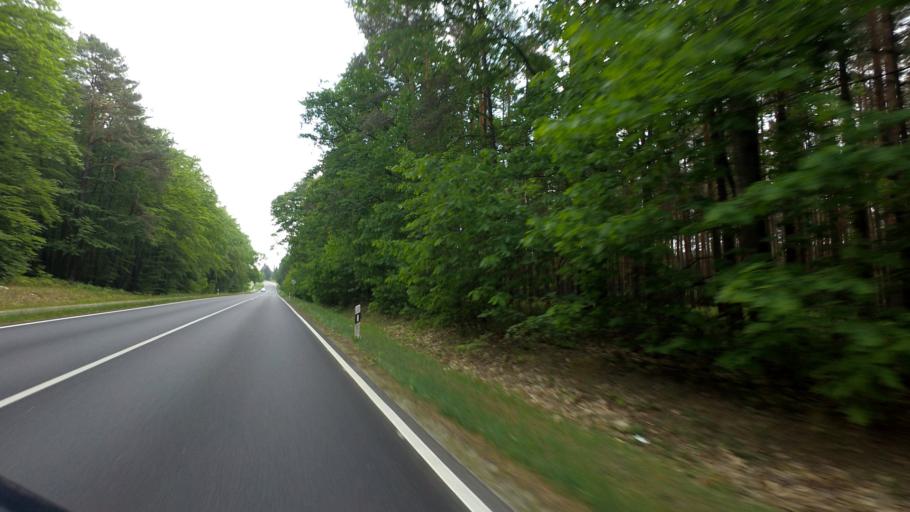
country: DE
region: Saxony
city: Rietschen
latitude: 51.3699
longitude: 14.7949
